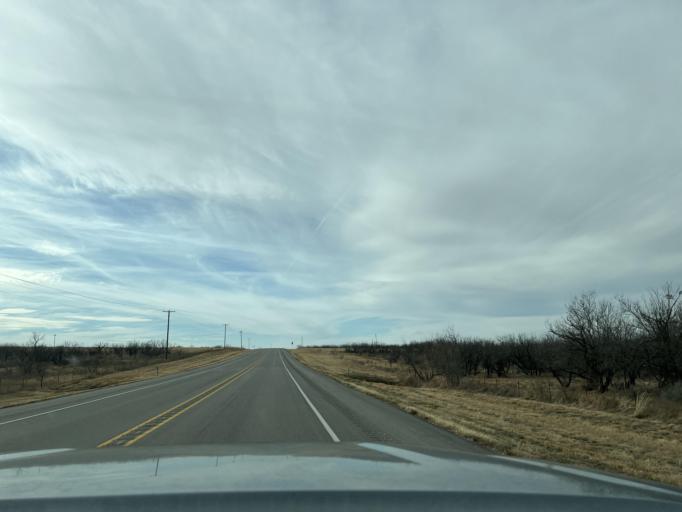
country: US
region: Texas
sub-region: Jones County
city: Anson
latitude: 32.7506
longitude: -99.6853
